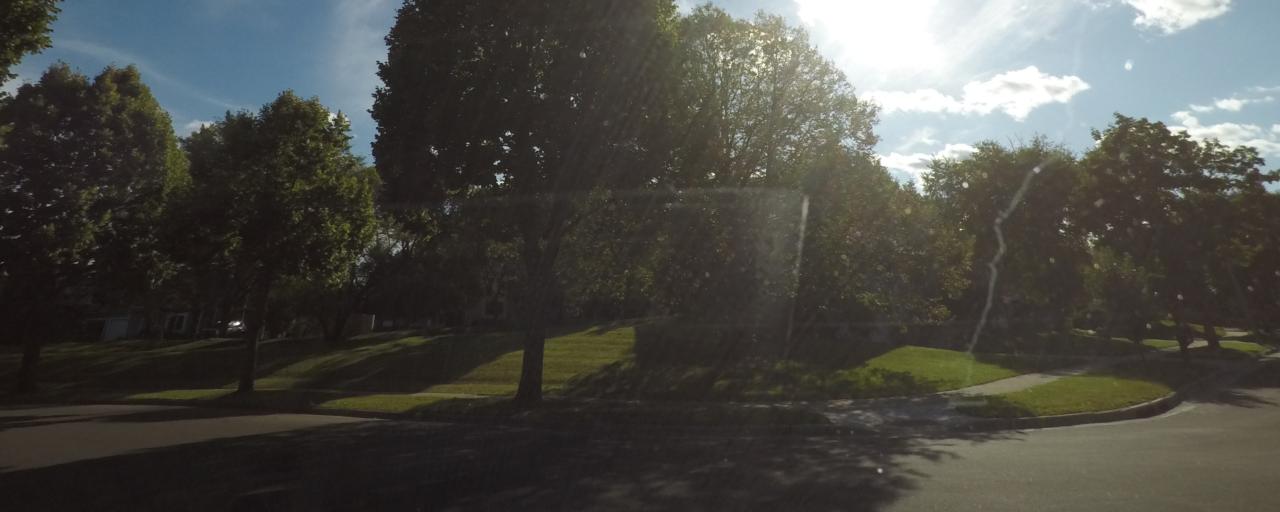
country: US
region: Wisconsin
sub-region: Dane County
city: Middleton
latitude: 43.0646
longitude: -89.5198
